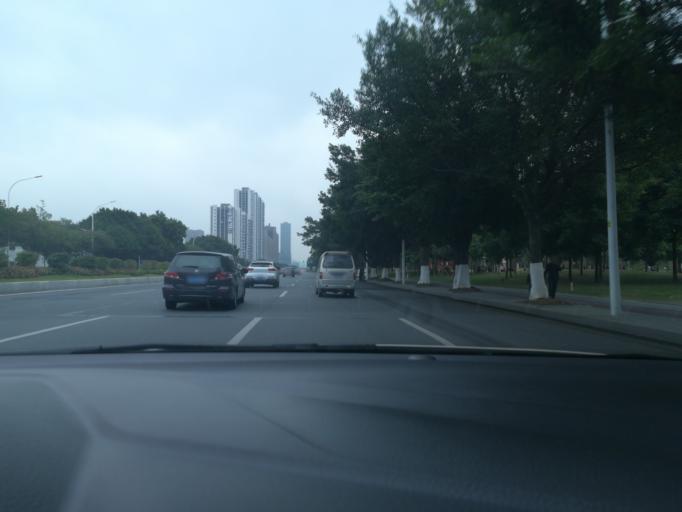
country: CN
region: Guangdong
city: Nansha
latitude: 22.8006
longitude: 113.5588
